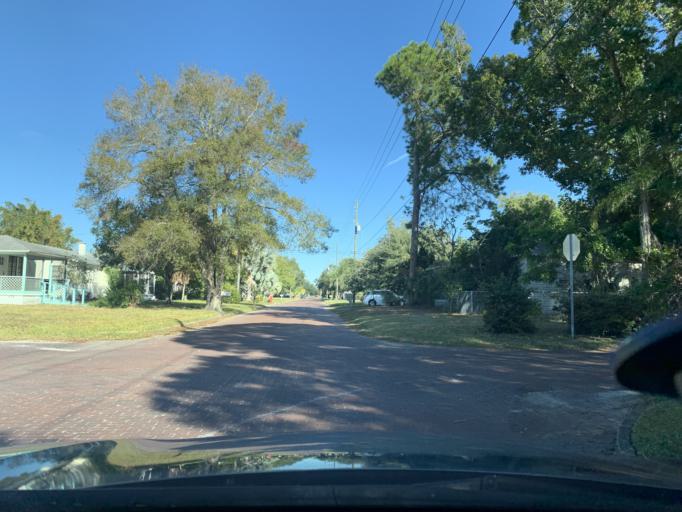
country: US
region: Florida
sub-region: Pinellas County
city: Gulfport
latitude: 27.7528
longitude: -82.7093
